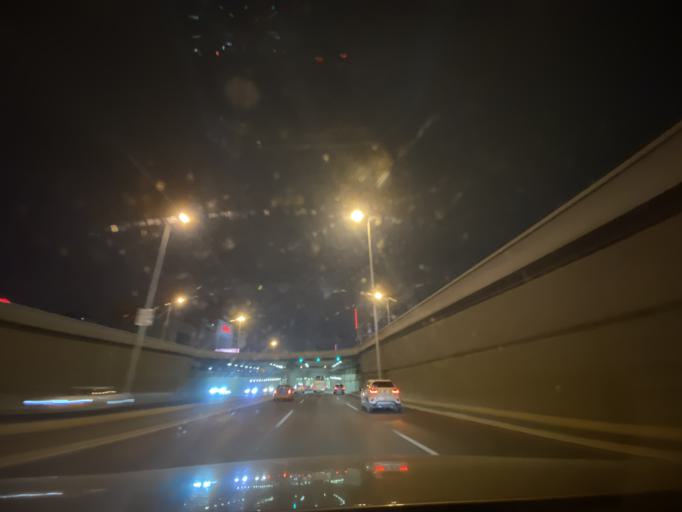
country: CN
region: Beijing
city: Baizhifang
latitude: 39.8959
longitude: 116.3197
